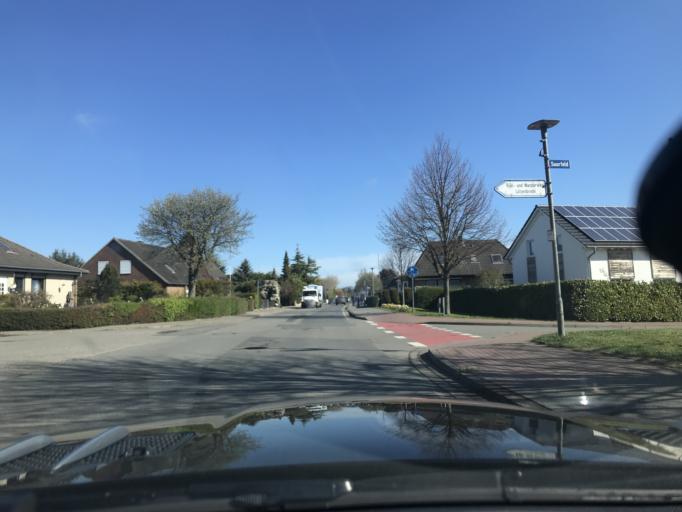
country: DE
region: Schleswig-Holstein
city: Grossenbrode
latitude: 54.3642
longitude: 11.0841
